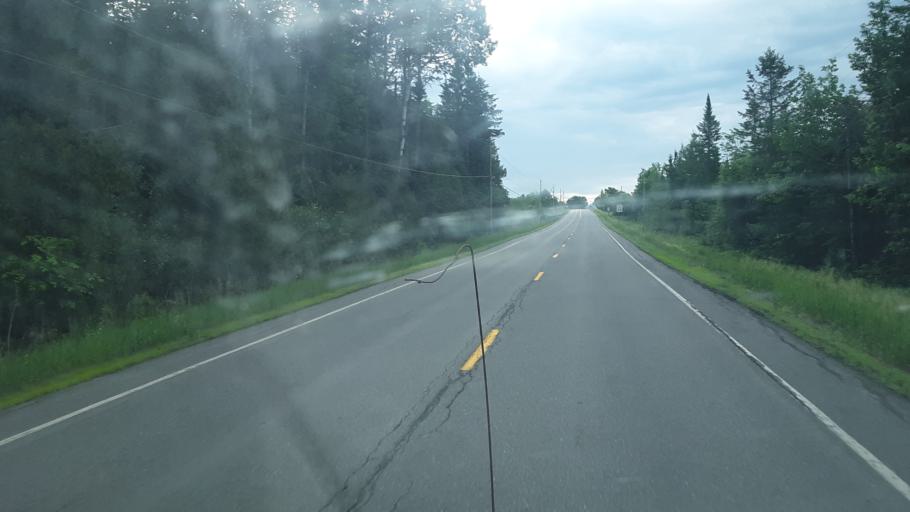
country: US
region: Maine
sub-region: Penobscot County
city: Patten
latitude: 45.8707
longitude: -68.3368
